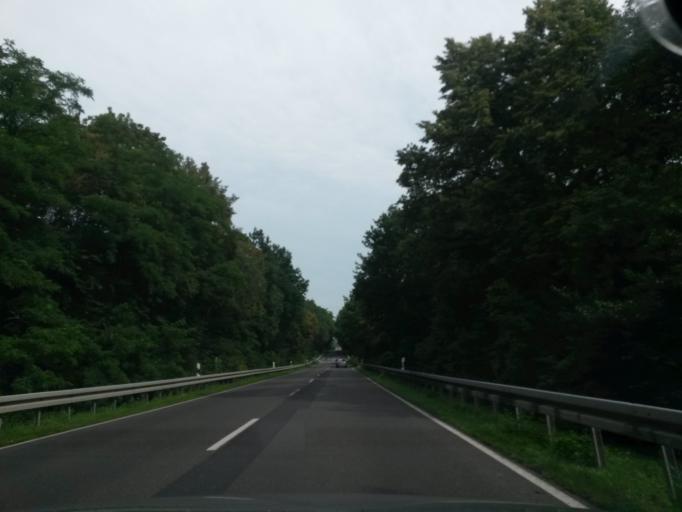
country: DE
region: Brandenburg
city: Meyenburg
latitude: 53.0289
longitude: 14.2173
